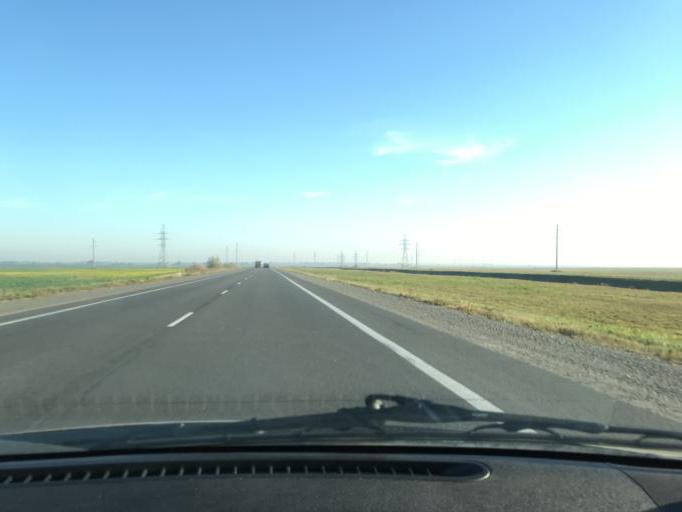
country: BY
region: Brest
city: Asnyezhytsy
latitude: 52.1952
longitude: 26.1062
